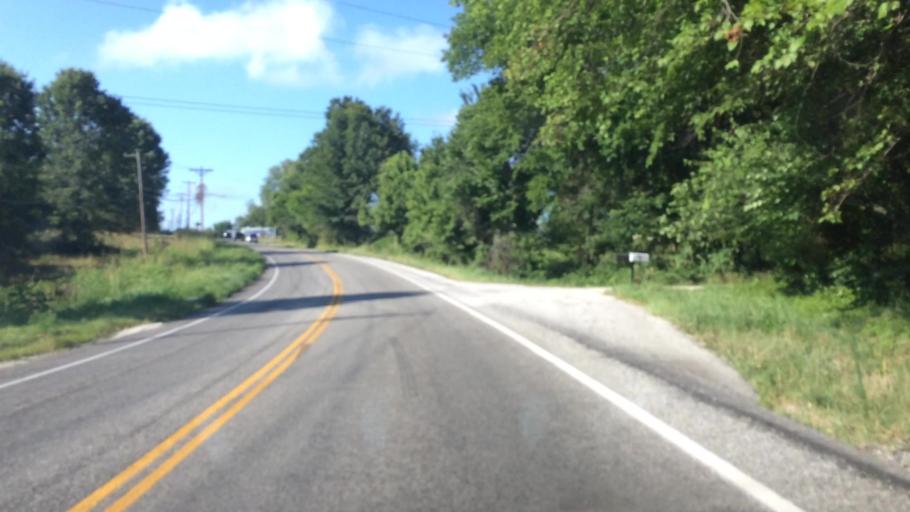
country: US
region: Missouri
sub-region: Greene County
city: Springfield
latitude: 37.2730
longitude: -93.2643
